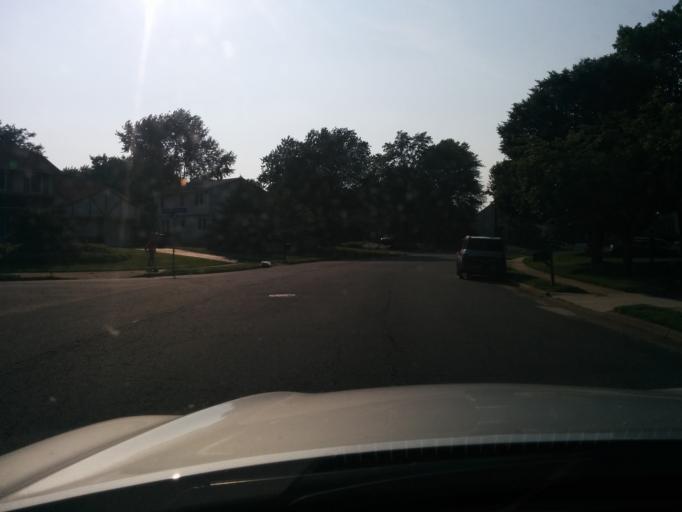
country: US
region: Virginia
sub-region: Fairfax County
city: Oak Hill
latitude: 38.9149
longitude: -77.4156
